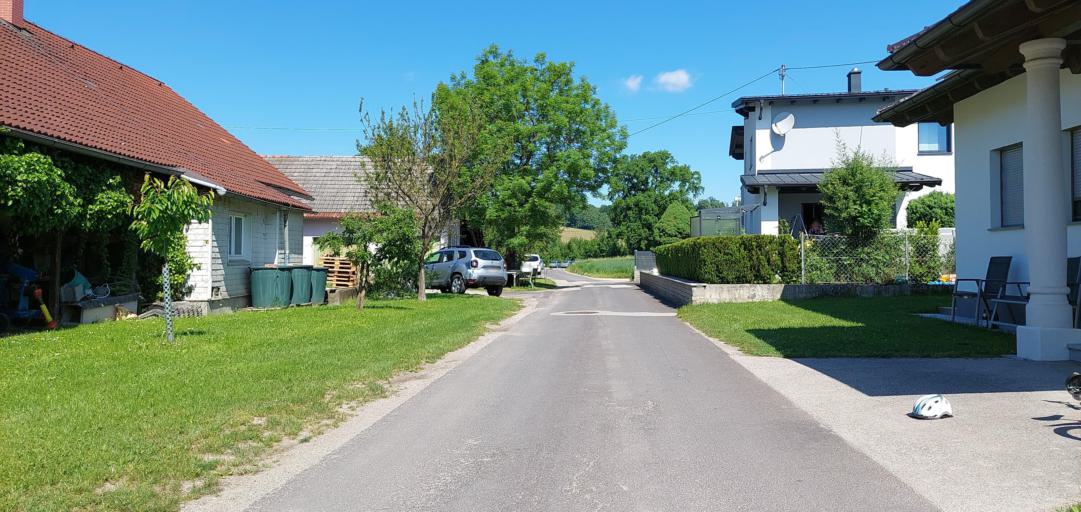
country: AT
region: Upper Austria
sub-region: Politischer Bezirk Grieskirchen
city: Bad Schallerbach
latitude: 48.2192
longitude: 13.9608
